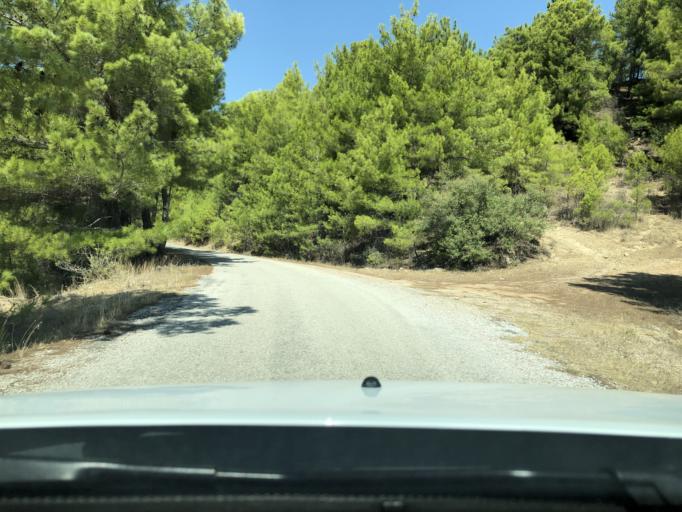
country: TR
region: Antalya
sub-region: Manavgat
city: Manavgat
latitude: 36.8391
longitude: 31.5331
